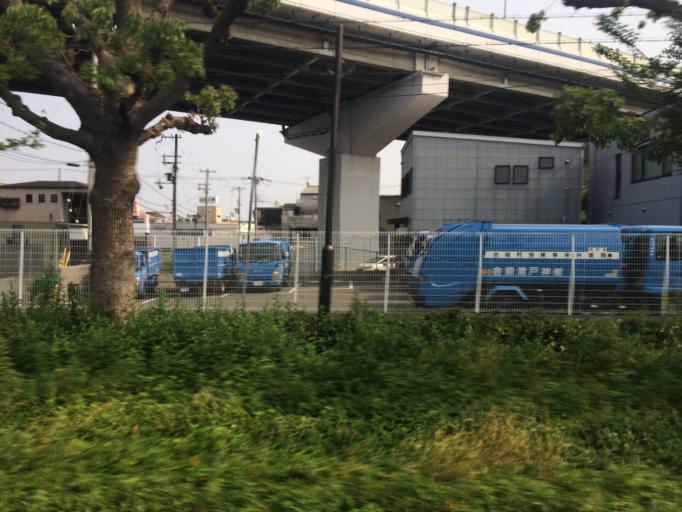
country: JP
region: Hyogo
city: Kobe
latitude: 34.7050
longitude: 135.2298
